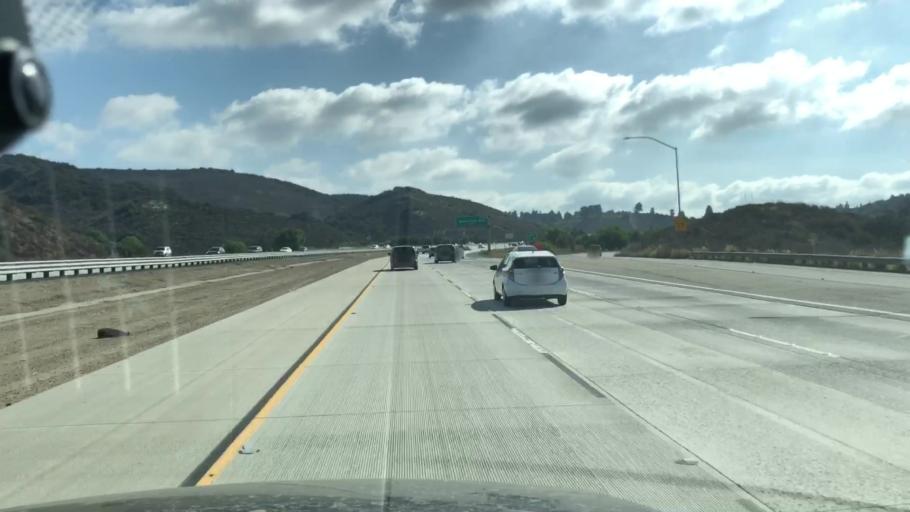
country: US
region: California
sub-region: Ventura County
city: Moorpark
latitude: 34.2448
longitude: -118.8398
